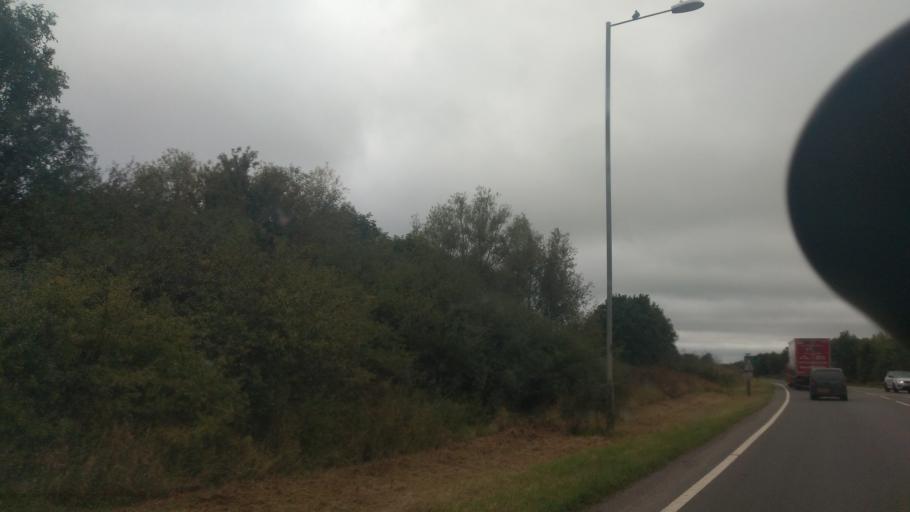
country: GB
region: England
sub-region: Wiltshire
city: Melksham
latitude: 51.3630
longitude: -2.1372
